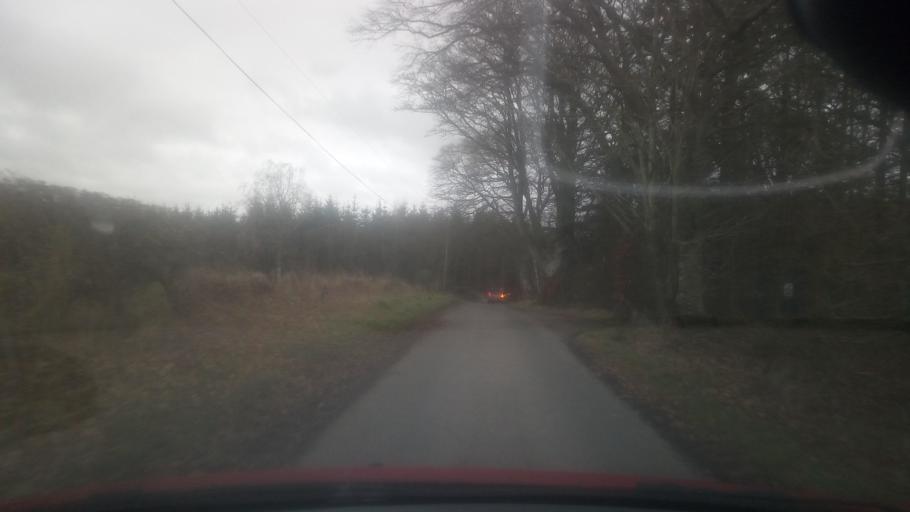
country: GB
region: Scotland
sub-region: The Scottish Borders
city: Jedburgh
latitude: 55.4657
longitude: -2.5230
